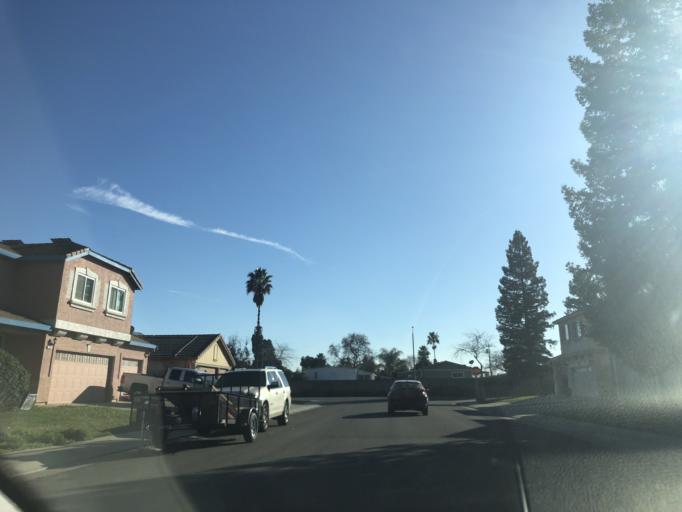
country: US
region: California
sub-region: Yolo County
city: Woodland
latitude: 38.6691
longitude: -121.7452
